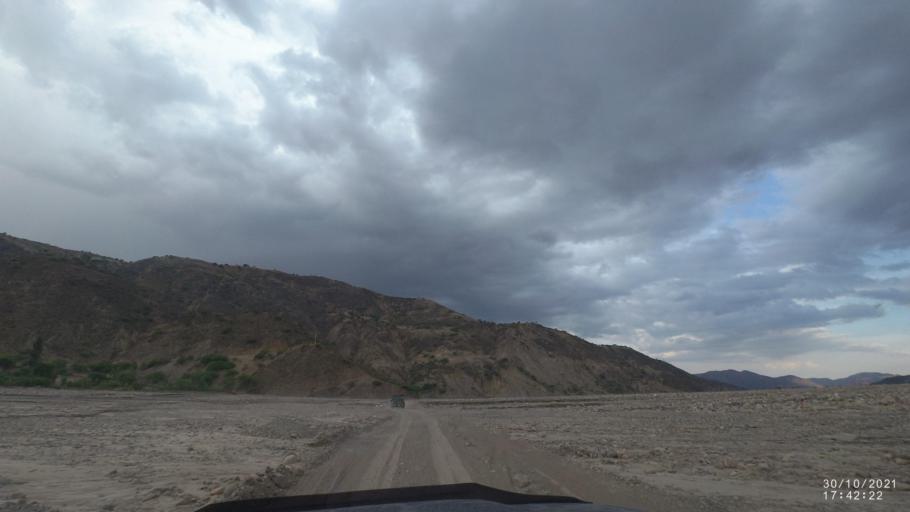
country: BO
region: Cochabamba
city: Sipe Sipe
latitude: -17.5264
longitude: -66.5431
